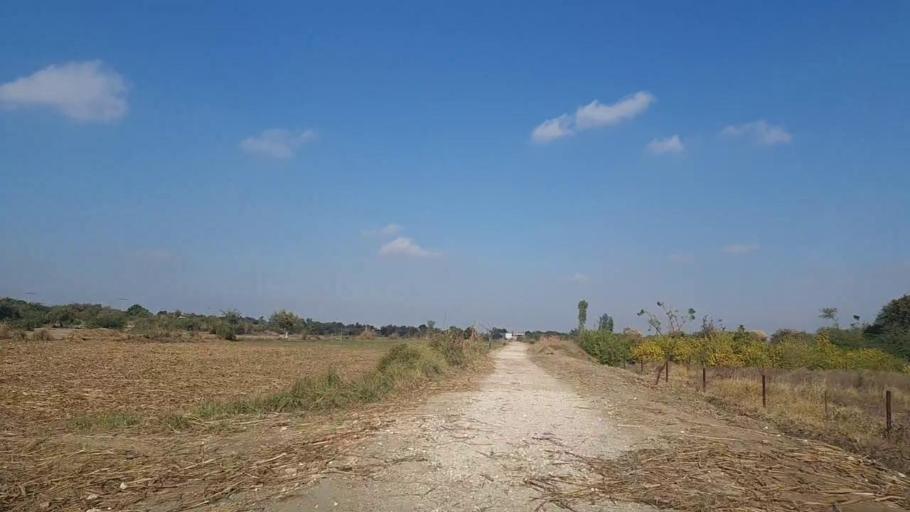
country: PK
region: Sindh
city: Tando Mittha Khan
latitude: 26.0036
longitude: 69.2593
